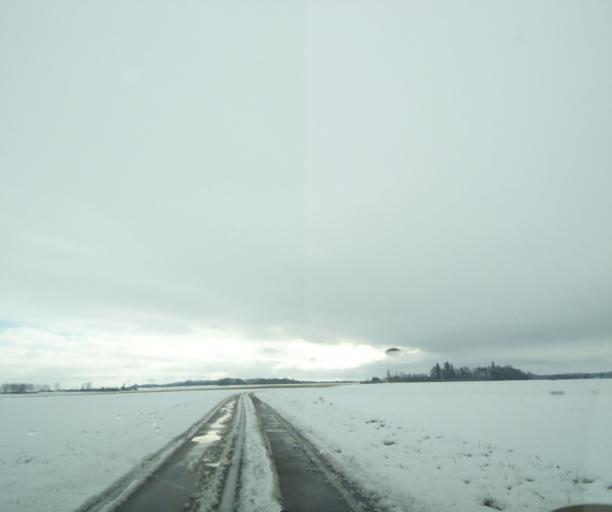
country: FR
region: Champagne-Ardenne
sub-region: Departement de la Haute-Marne
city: Montier-en-Der
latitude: 48.4617
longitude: 4.6504
